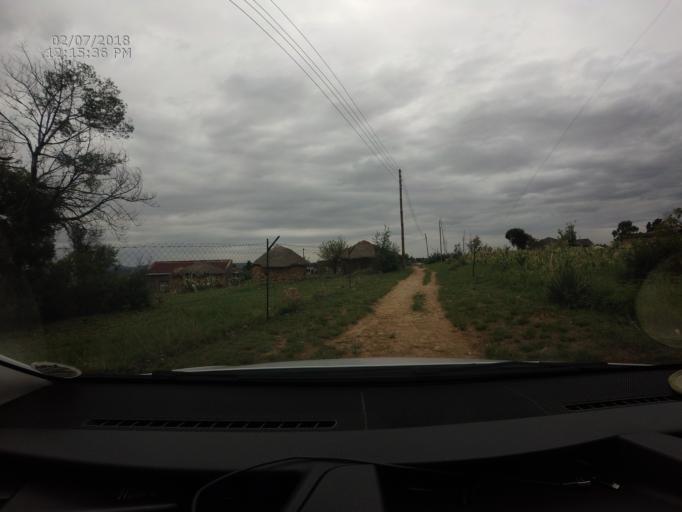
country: LS
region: Berea
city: Teyateyaneng
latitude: -29.1195
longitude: 27.9597
